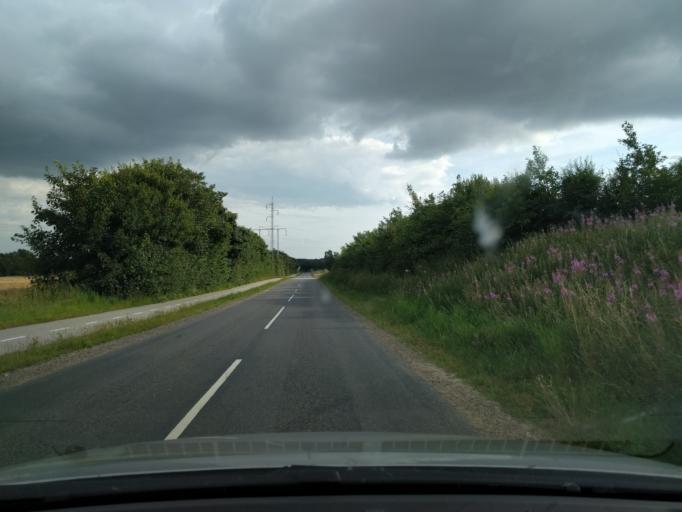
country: DK
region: Central Jutland
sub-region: Herning Kommune
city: Snejbjerg
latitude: 56.1107
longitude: 8.9079
